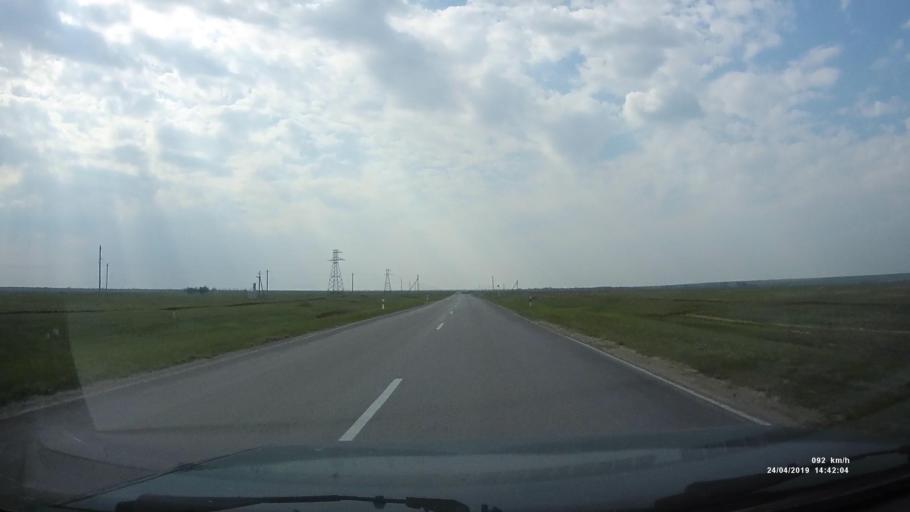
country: RU
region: Rostov
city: Remontnoye
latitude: 46.4501
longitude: 43.8694
